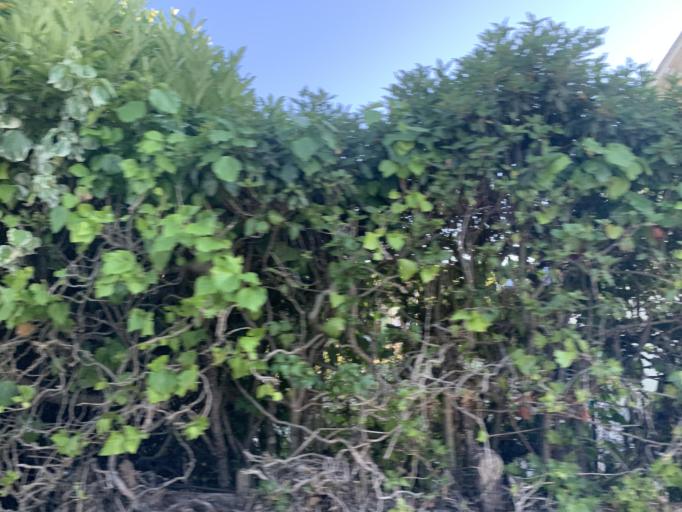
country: FR
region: Pays de la Loire
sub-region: Departement de la Loire-Atlantique
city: Pornichet
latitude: 47.2561
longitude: -2.3210
